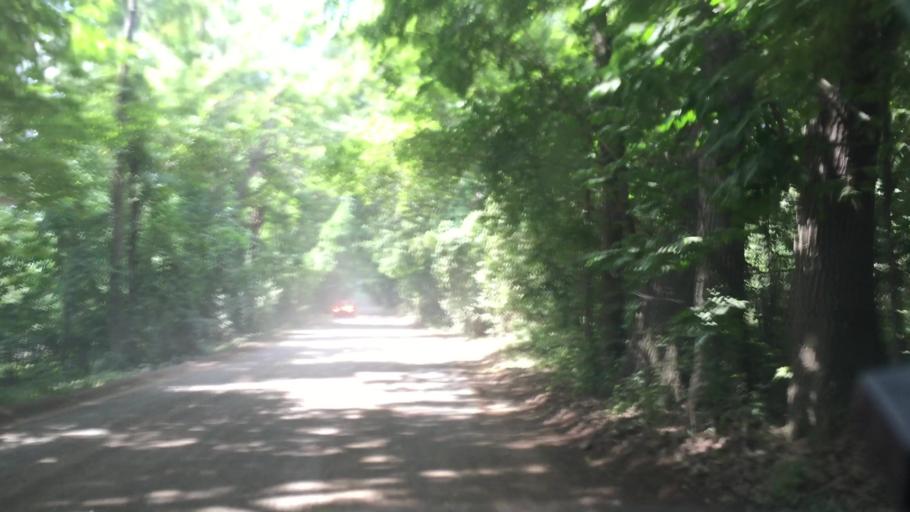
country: US
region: Michigan
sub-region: Oakland County
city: Auburn Hills
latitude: 42.6541
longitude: -83.2162
